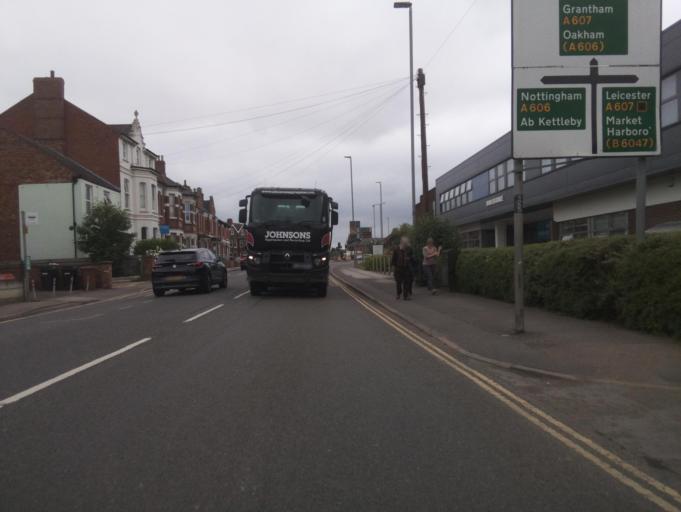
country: GB
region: England
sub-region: Leicestershire
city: Melton Mowbray
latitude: 52.7668
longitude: -0.8918
